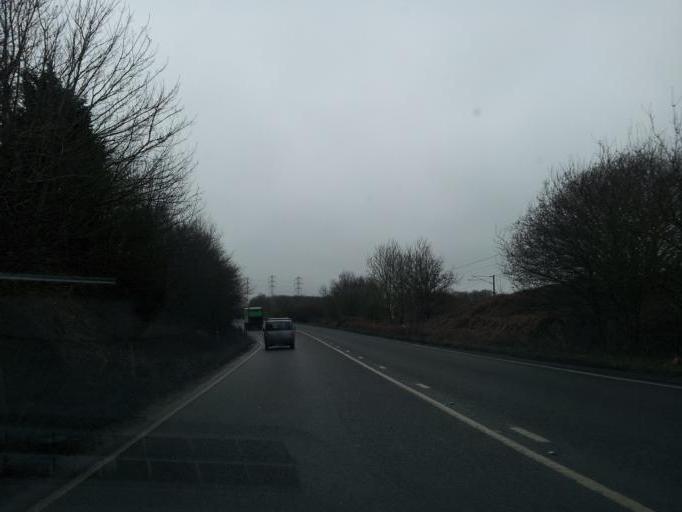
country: GB
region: England
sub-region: Suffolk
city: Ipswich
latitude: 52.0316
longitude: 1.1445
